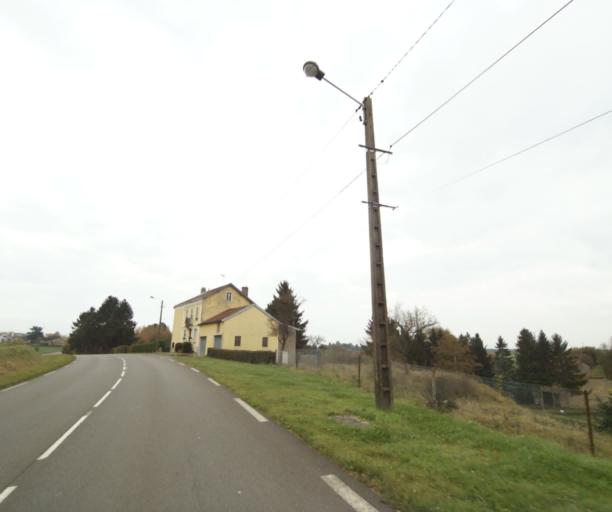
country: FR
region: Lorraine
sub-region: Departement de Meurthe-et-Moselle
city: Mancieulles
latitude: 49.2902
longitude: 5.8889
